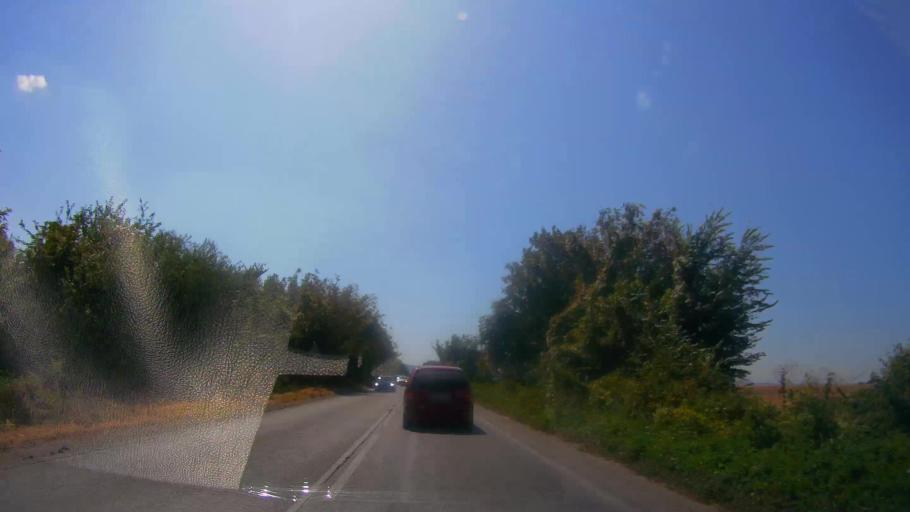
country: BG
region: Veliko Turnovo
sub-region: Obshtina Gorna Oryakhovitsa
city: Purvomaytsi
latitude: 43.2347
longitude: 25.6405
